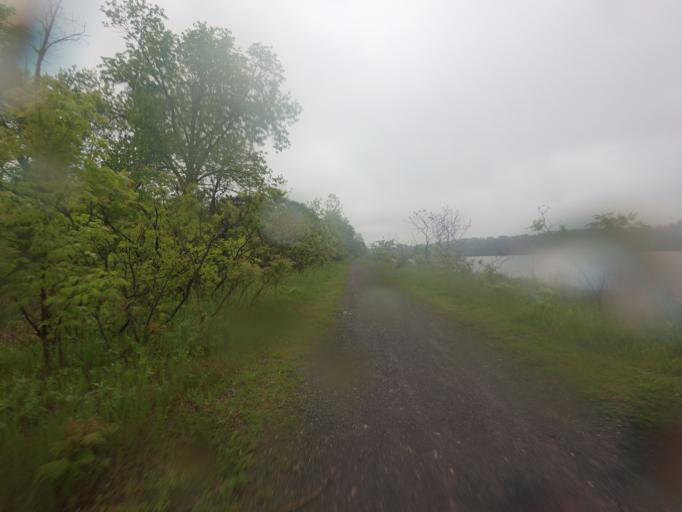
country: CA
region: Ontario
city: Kingston
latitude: 44.4155
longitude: -76.5880
